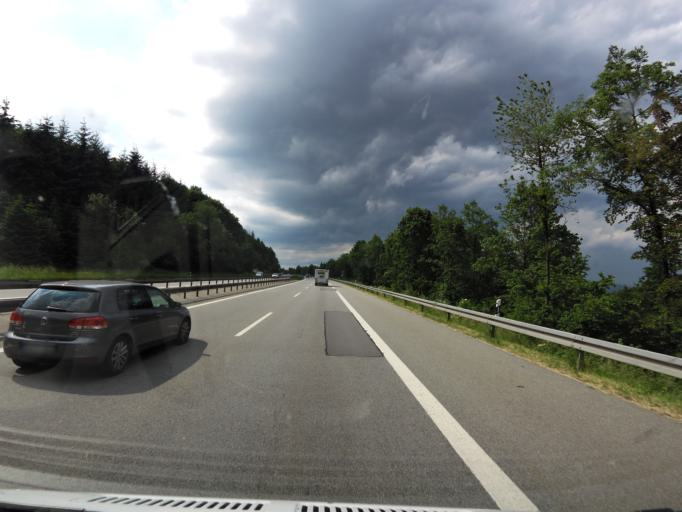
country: DE
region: Bavaria
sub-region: Lower Bavaria
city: Aussernzell
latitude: 48.6826
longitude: 13.2186
